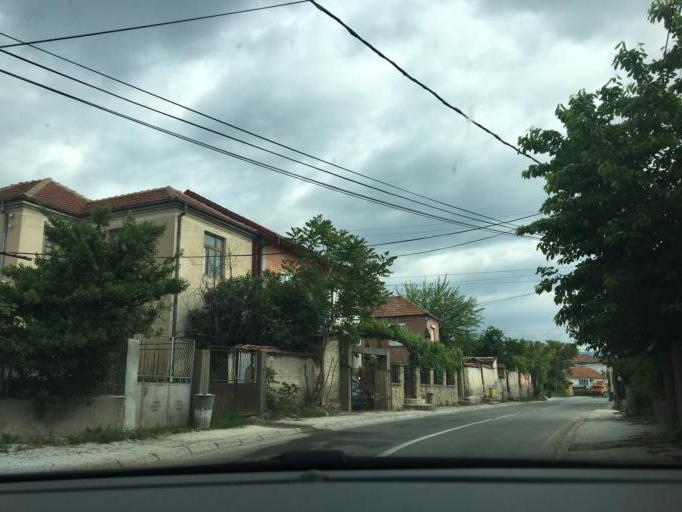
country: MK
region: Resen
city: Resen
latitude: 41.0902
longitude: 21.0094
